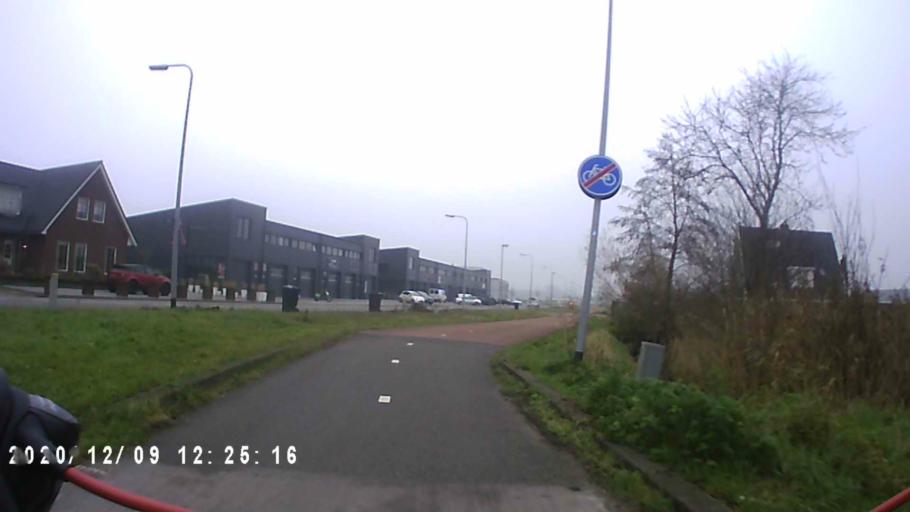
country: NL
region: Groningen
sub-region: Gemeente Haren
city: Haren
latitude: 53.2084
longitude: 6.6221
